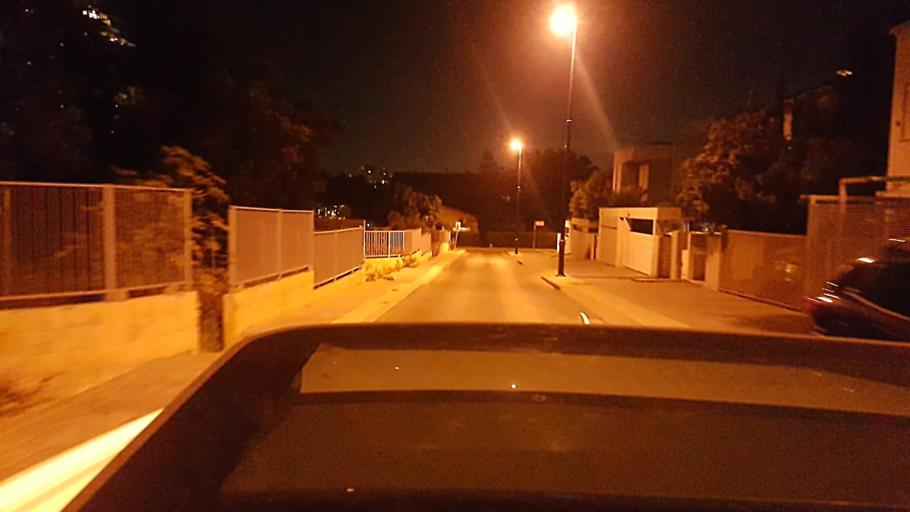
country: IL
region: Central District
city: Hod HaSharon
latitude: 32.1635
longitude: 34.8915
